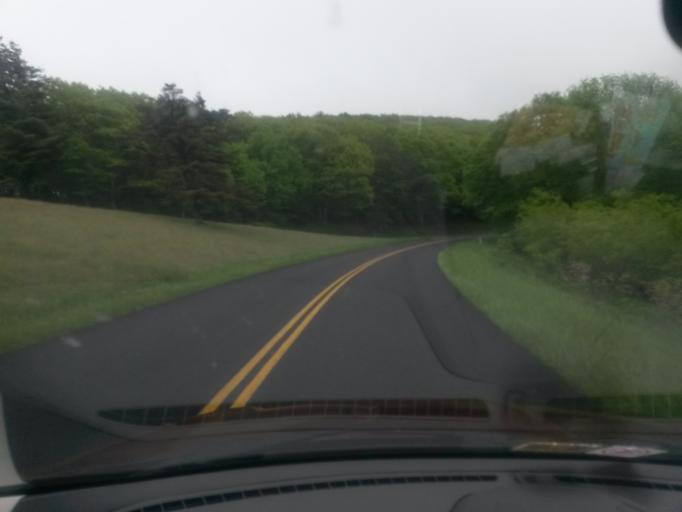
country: US
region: Virginia
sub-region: Floyd County
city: Floyd
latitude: 36.8231
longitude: -80.3425
